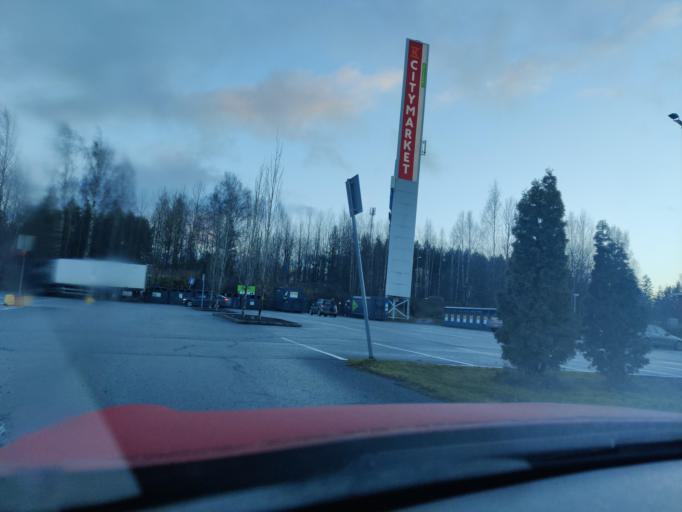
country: FI
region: Pirkanmaa
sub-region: Tampere
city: Nokia
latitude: 61.4661
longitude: 23.5082
